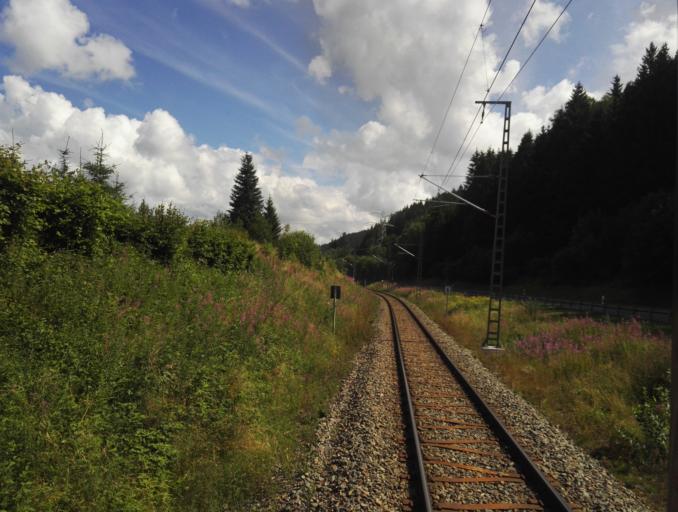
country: DE
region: Baden-Wuerttemberg
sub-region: Freiburg Region
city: Titisee-Neustadt
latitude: 47.9010
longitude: 8.1639
